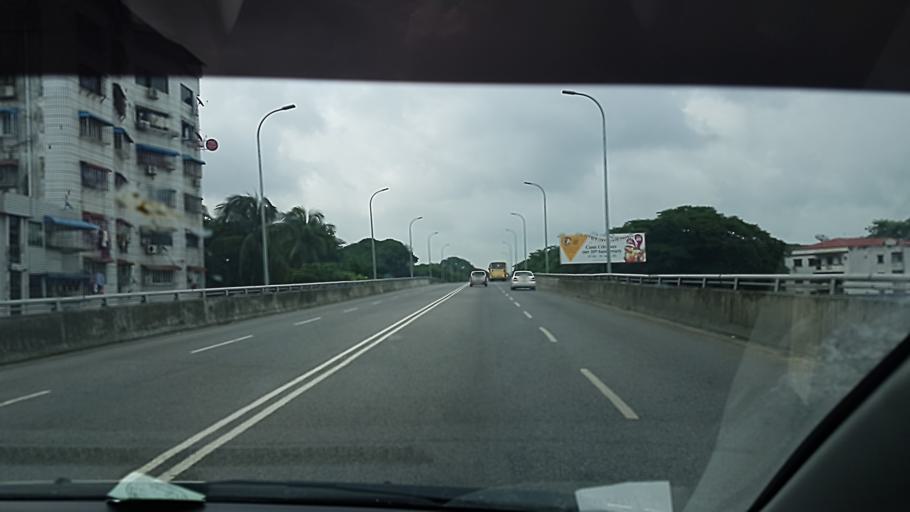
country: MM
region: Yangon
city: Yangon
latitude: 16.8026
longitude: 96.1377
